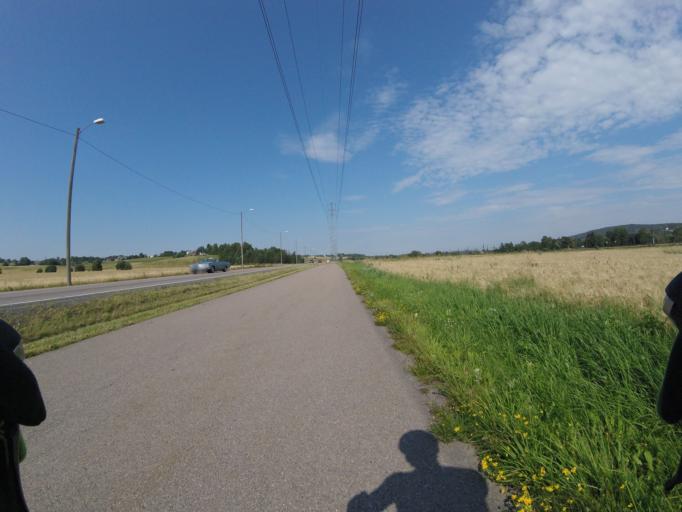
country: NO
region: Akershus
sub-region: Skedsmo
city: Leirsund
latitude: 59.9801
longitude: 11.0698
